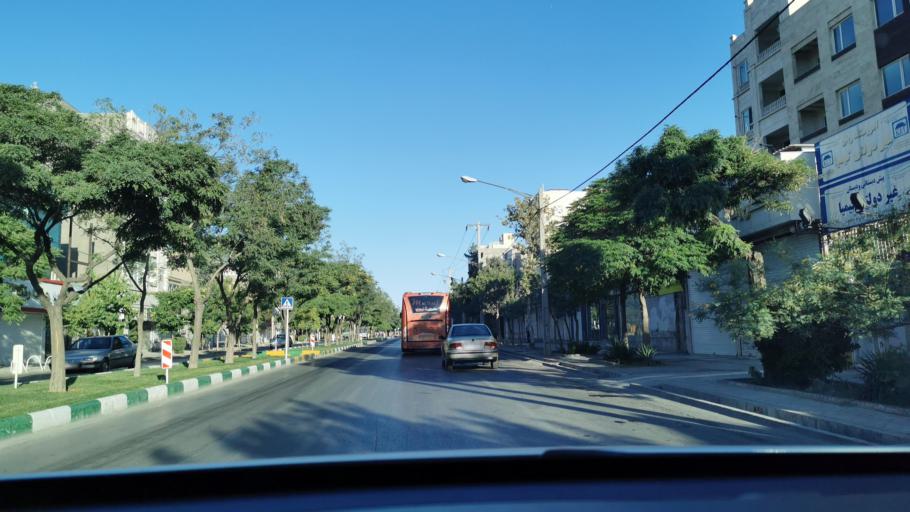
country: IR
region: Razavi Khorasan
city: Mashhad
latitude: 36.3523
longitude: 59.4967
